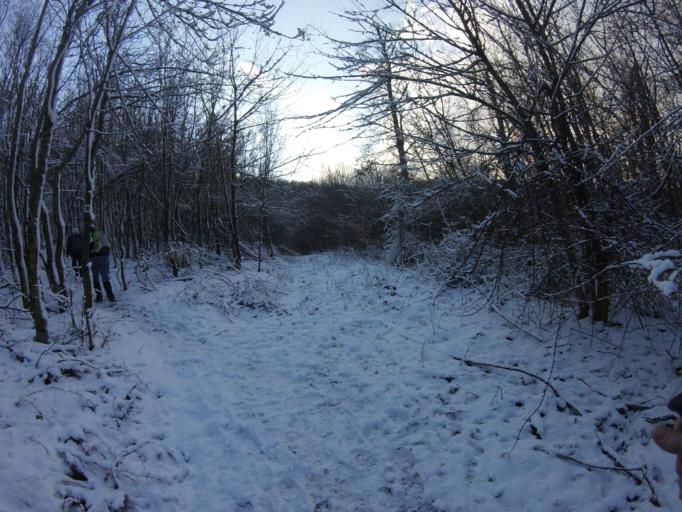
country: HU
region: Pest
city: Pilisszentkereszt
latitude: 47.7233
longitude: 18.9027
